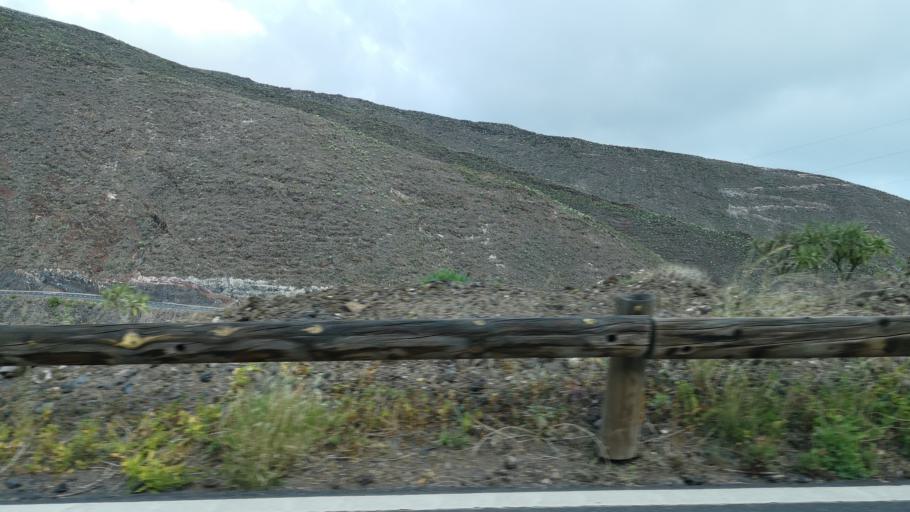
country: ES
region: Canary Islands
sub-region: Provincia de Santa Cruz de Tenerife
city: San Sebastian de la Gomera
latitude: 28.0850
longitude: -17.1259
